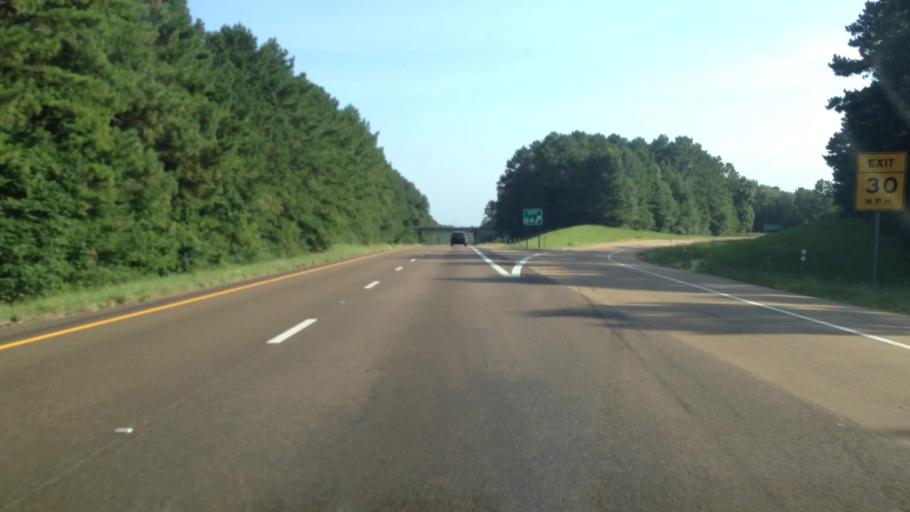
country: US
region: Mississippi
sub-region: Pike County
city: Summit
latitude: 31.3459
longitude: -90.4783
